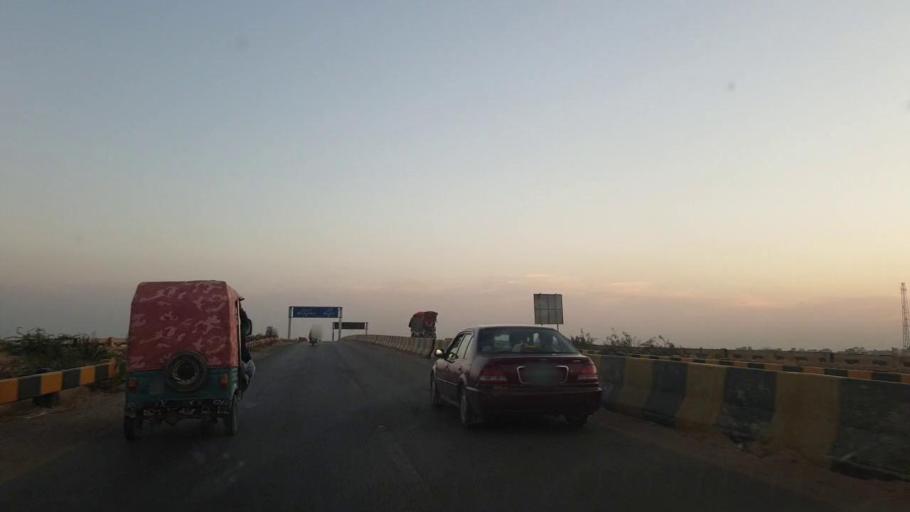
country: PK
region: Sindh
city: Jamshoro
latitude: 25.4015
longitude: 68.2724
